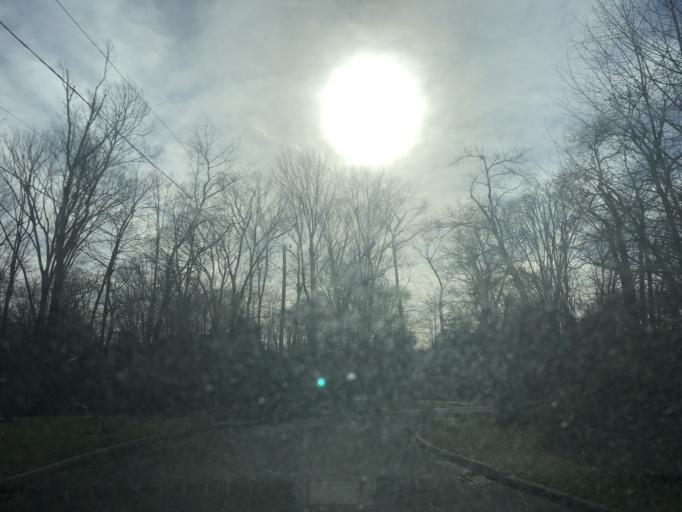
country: US
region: New Jersey
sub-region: Somerset County
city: Kingston
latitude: 40.3558
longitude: -74.6310
